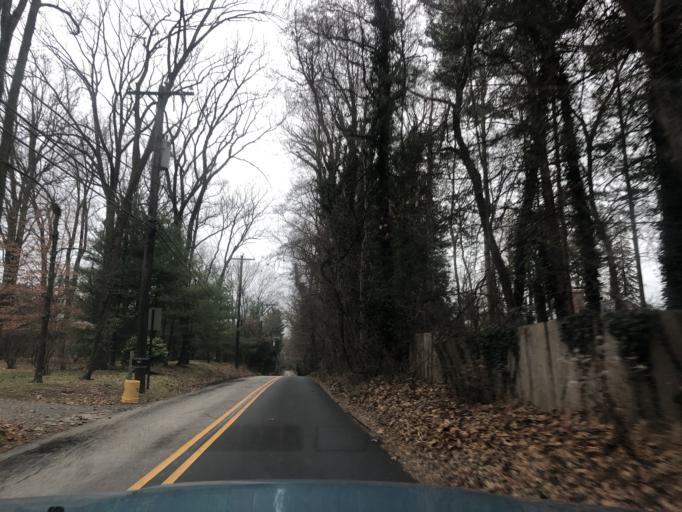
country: US
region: Pennsylvania
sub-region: Delaware County
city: Radnor
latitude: 40.0273
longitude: -75.3538
